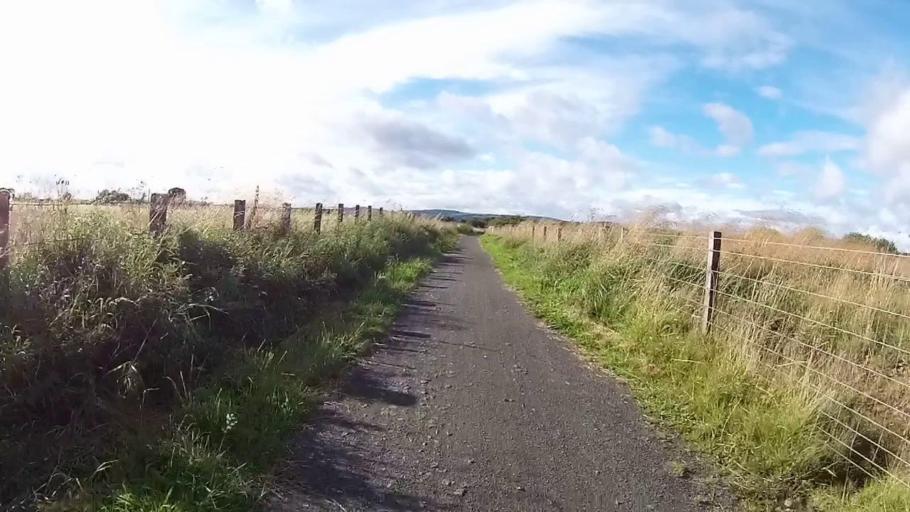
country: GB
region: Scotland
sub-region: Perth and Kinross
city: Kinross
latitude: 56.1932
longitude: -3.4149
